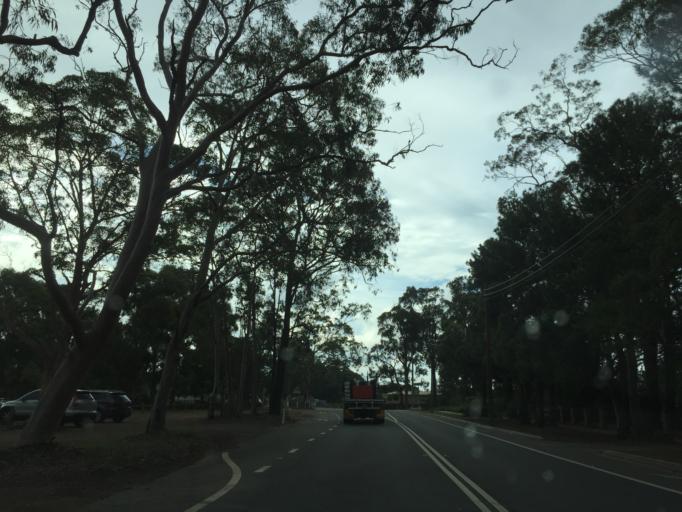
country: AU
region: New South Wales
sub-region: Hornsby Shire
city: Galston
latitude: -33.6587
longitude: 151.0401
